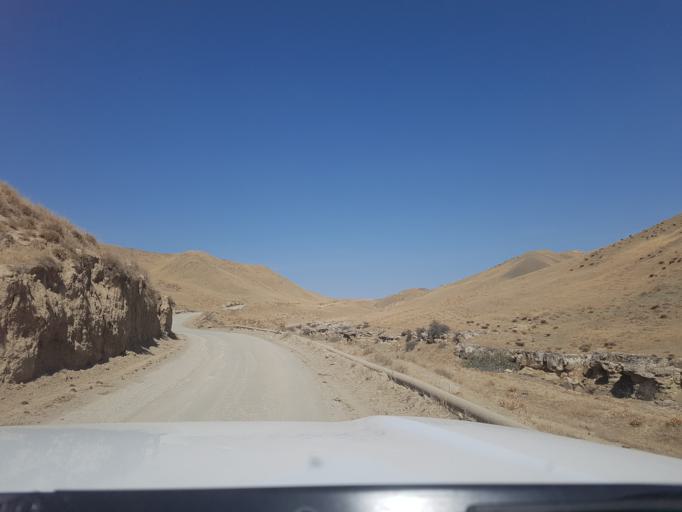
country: TM
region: Ahal
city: Baharly
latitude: 38.2557
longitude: 56.8897
